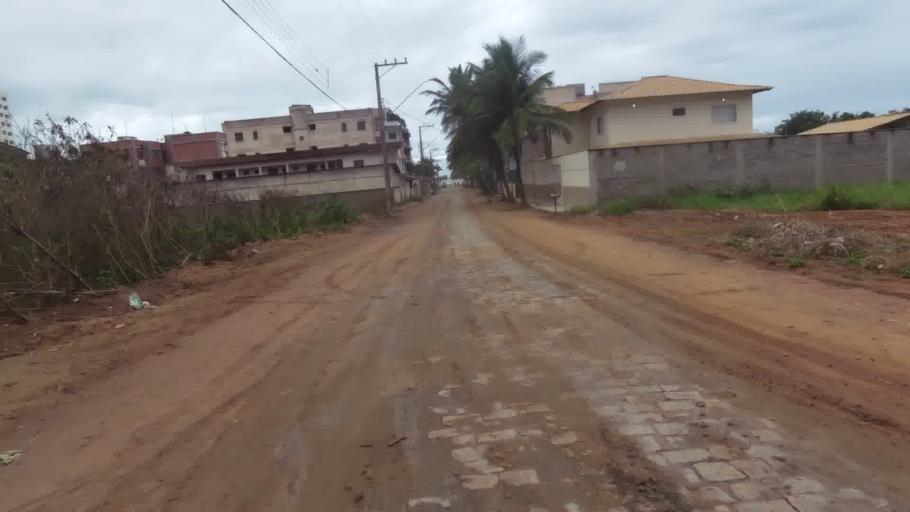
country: BR
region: Espirito Santo
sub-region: Marataizes
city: Marataizes
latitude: -21.0562
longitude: -40.8352
